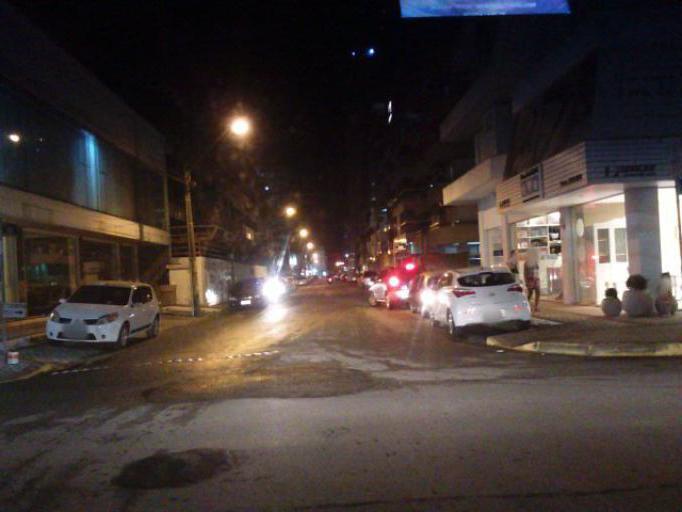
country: BR
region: Santa Catarina
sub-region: Itapema
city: Itapema
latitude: -27.1318
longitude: -48.6025
